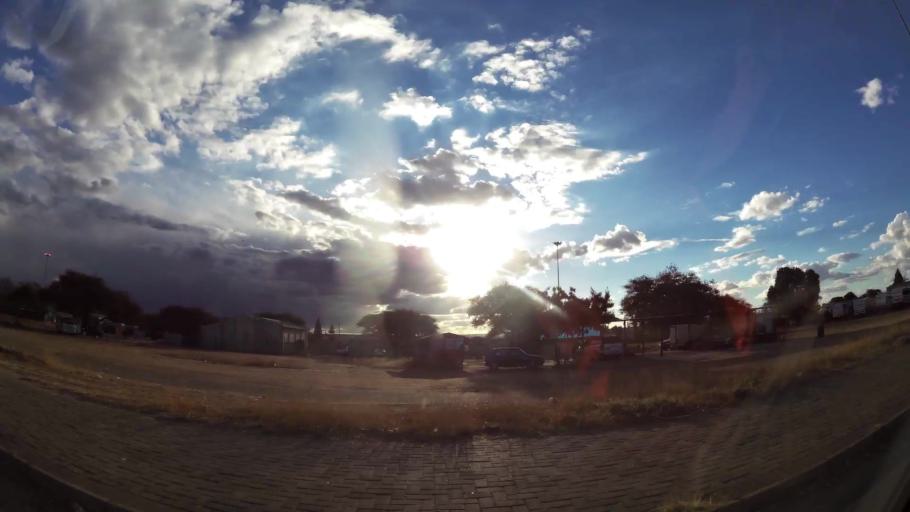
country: ZA
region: Limpopo
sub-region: Capricorn District Municipality
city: Polokwane
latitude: -23.9033
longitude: 29.4310
